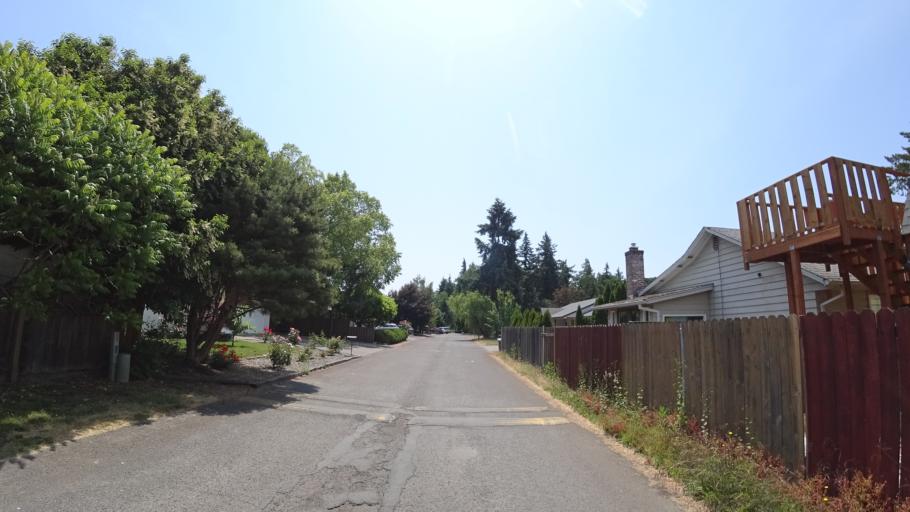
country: US
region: Oregon
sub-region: Washington County
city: Hillsboro
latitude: 45.4993
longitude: -122.9348
